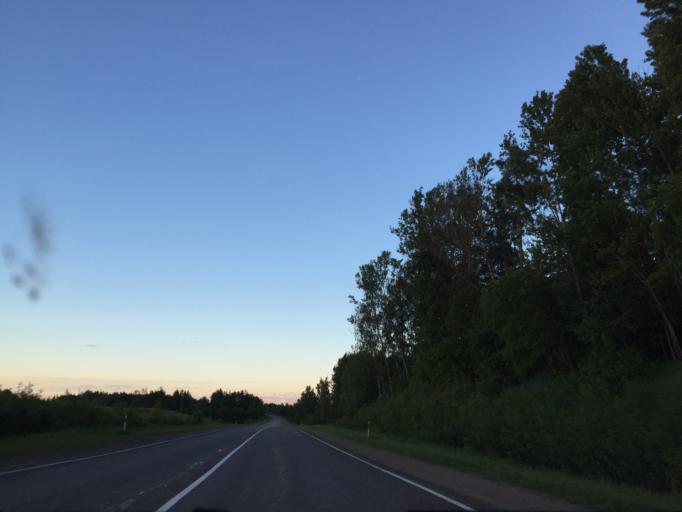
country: LV
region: Smiltene
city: Smiltene
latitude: 57.4241
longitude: 26.1219
